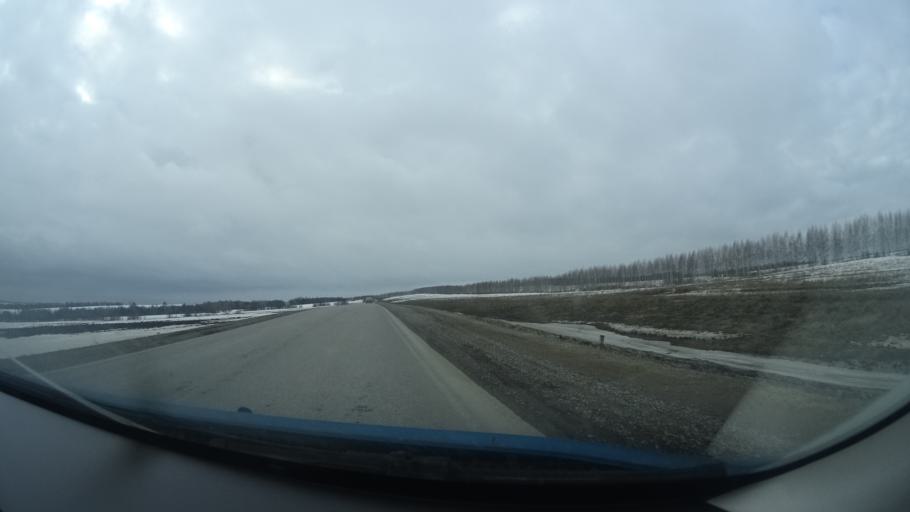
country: RU
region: Bashkortostan
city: Birsk
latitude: 55.3824
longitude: 55.5803
